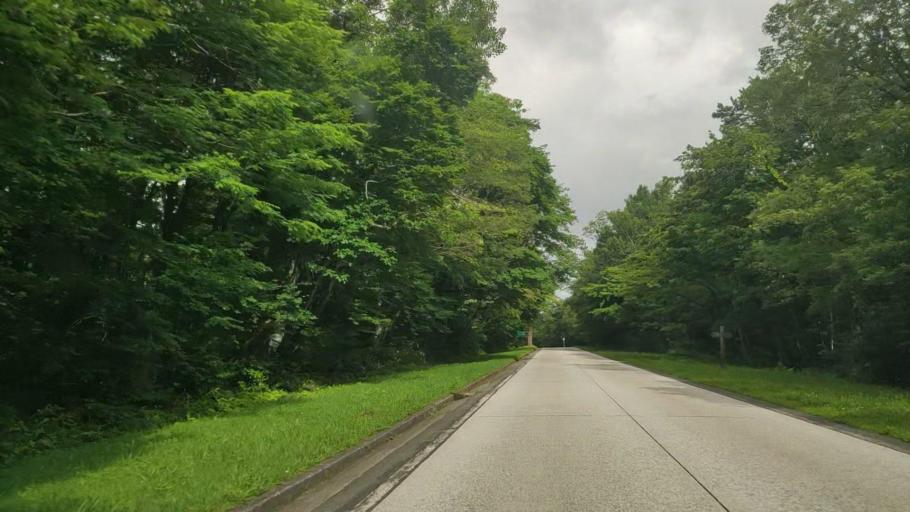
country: JP
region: Tottori
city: Yonago
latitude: 35.3969
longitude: 133.5147
